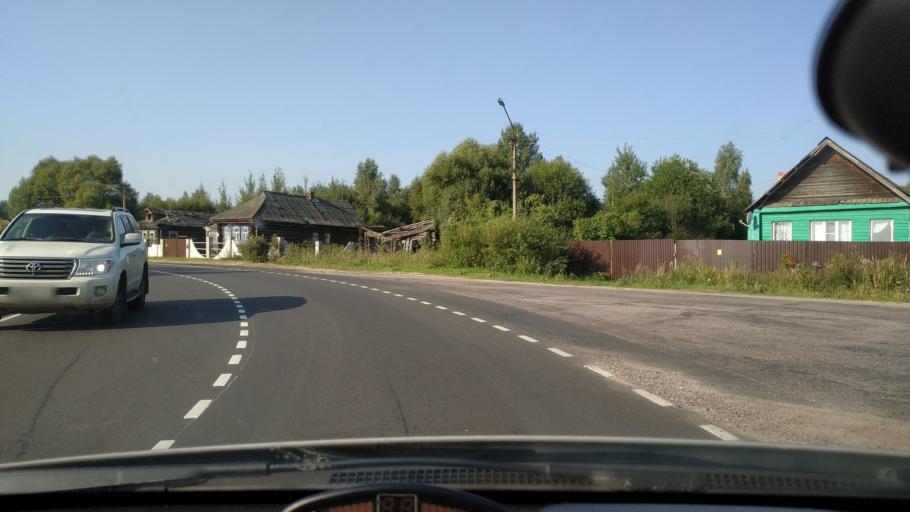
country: RU
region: Moskovskaya
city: Misheronskiy
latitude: 55.6574
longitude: 39.7521
